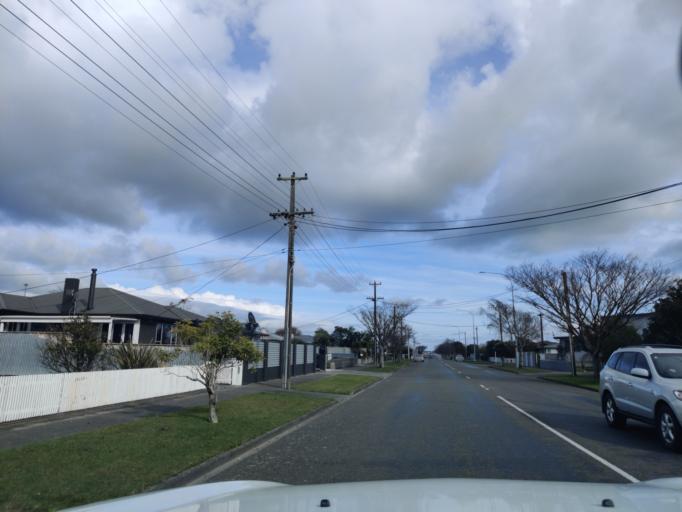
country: NZ
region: Manawatu-Wanganui
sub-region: Palmerston North City
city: Palmerston North
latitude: -40.3343
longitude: 175.6109
